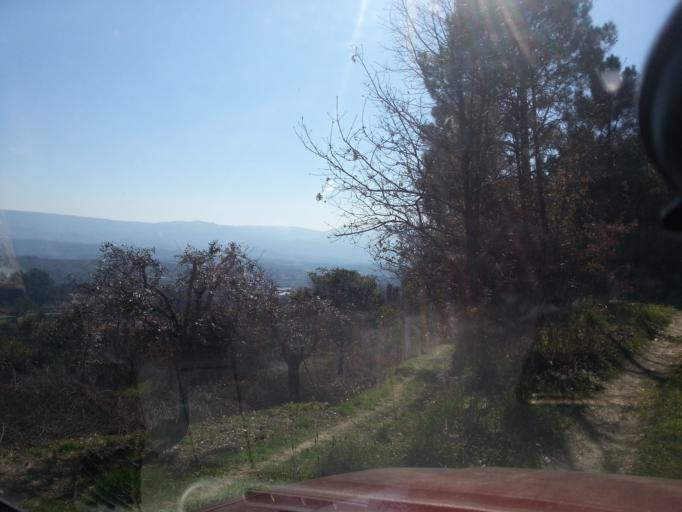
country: PT
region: Guarda
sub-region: Fornos de Algodres
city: Fornos de Algodres
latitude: 40.6270
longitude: -7.5361
